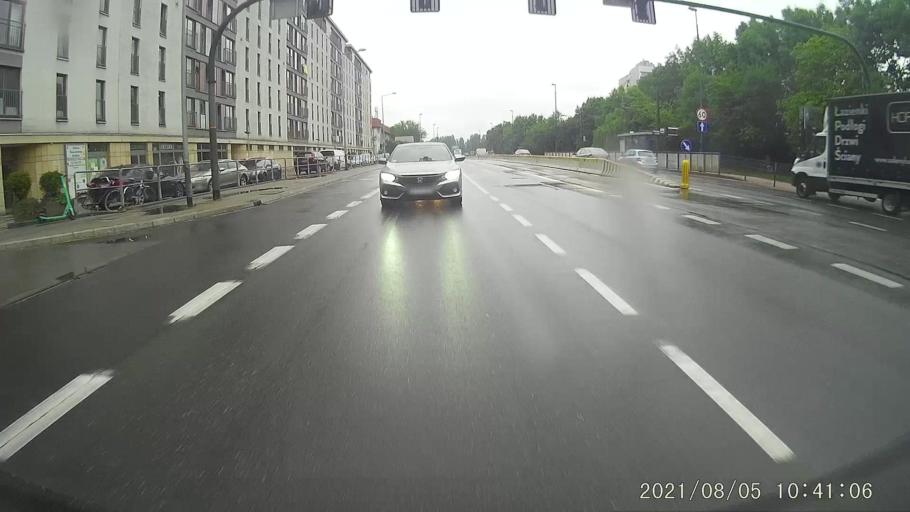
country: PL
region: Lesser Poland Voivodeship
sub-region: Krakow
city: Krakow
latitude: 50.0411
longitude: 19.9240
